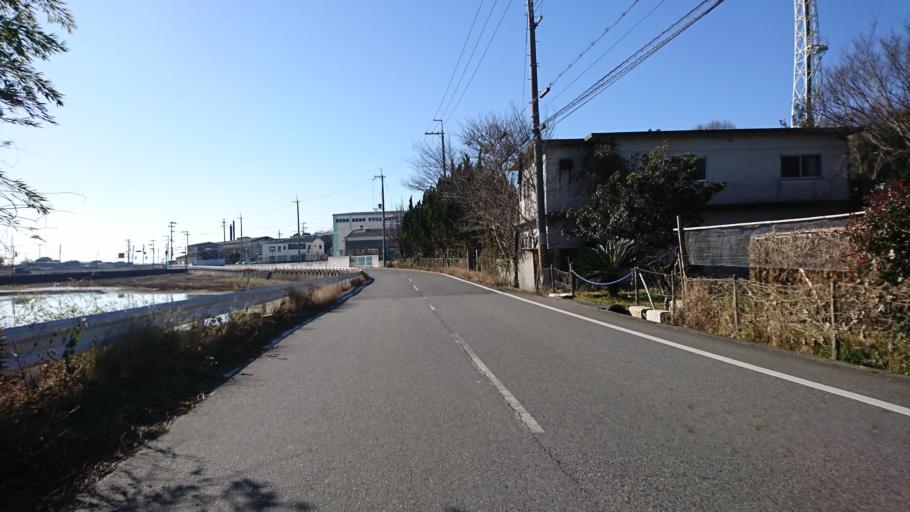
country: JP
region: Hyogo
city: Miki
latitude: 34.7535
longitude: 134.9259
